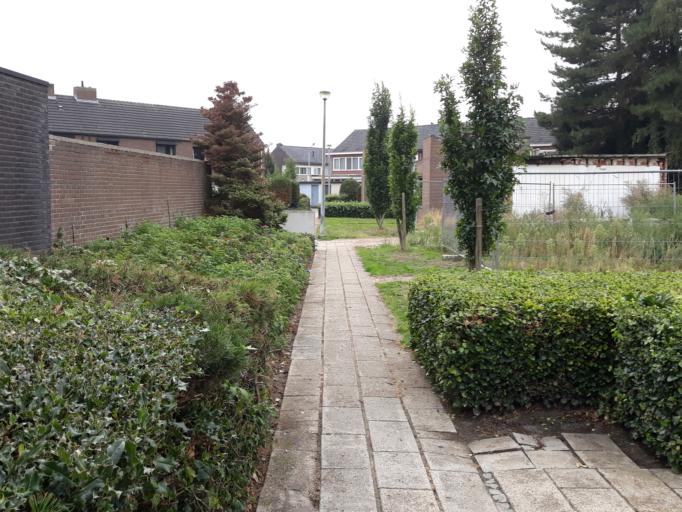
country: BE
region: Flanders
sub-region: Provincie Antwerpen
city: Vosselaar
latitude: 51.3107
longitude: 4.8894
